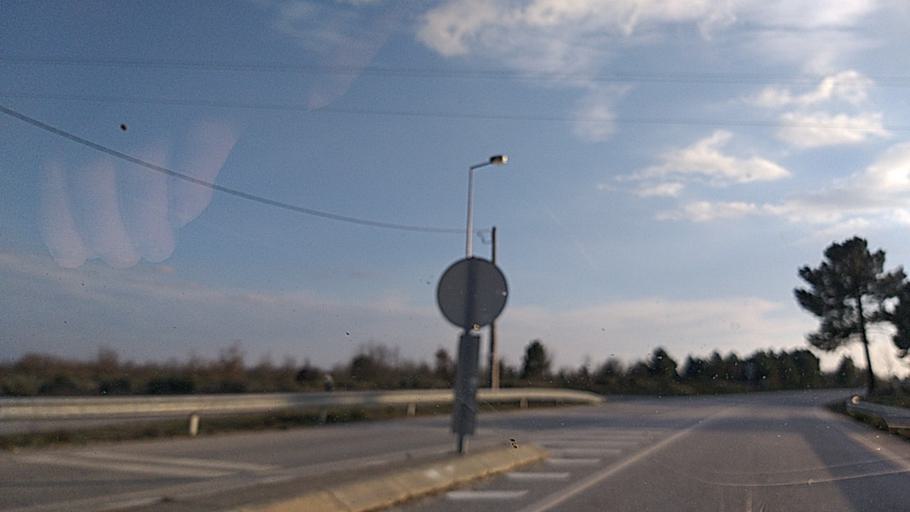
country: ES
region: Castille and Leon
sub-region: Provincia de Salamanca
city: Fuentes de Onoro
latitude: 40.6062
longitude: -6.9834
